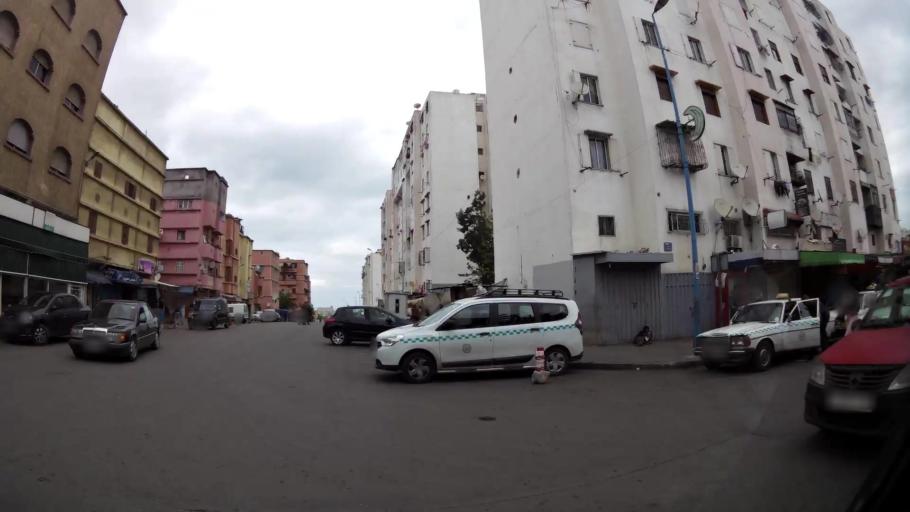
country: MA
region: Grand Casablanca
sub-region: Casablanca
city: Casablanca
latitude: 33.5858
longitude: -7.5575
